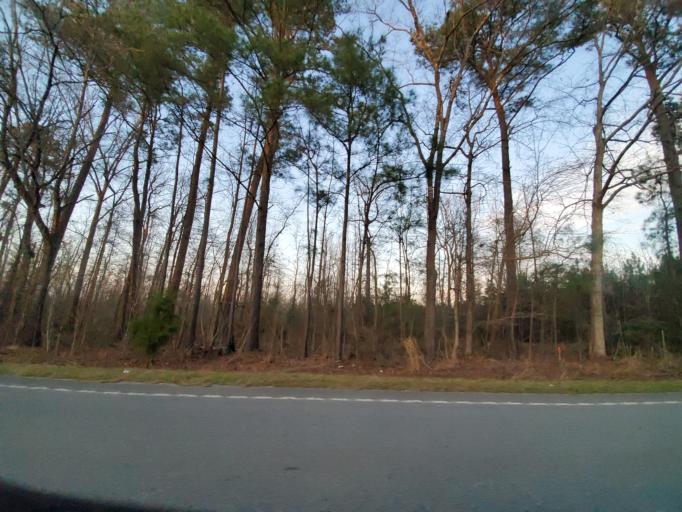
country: US
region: South Carolina
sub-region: Dorchester County
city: Ridgeville
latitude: 33.0034
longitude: -80.3241
